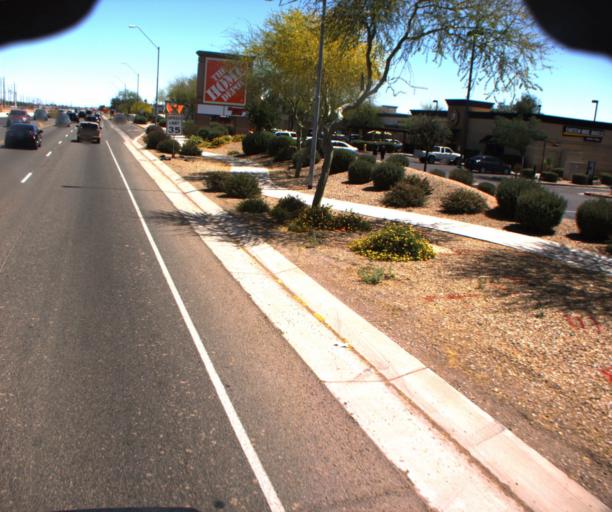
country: US
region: Arizona
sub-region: Maricopa County
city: Sun City West
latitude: 33.6420
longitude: -112.3549
